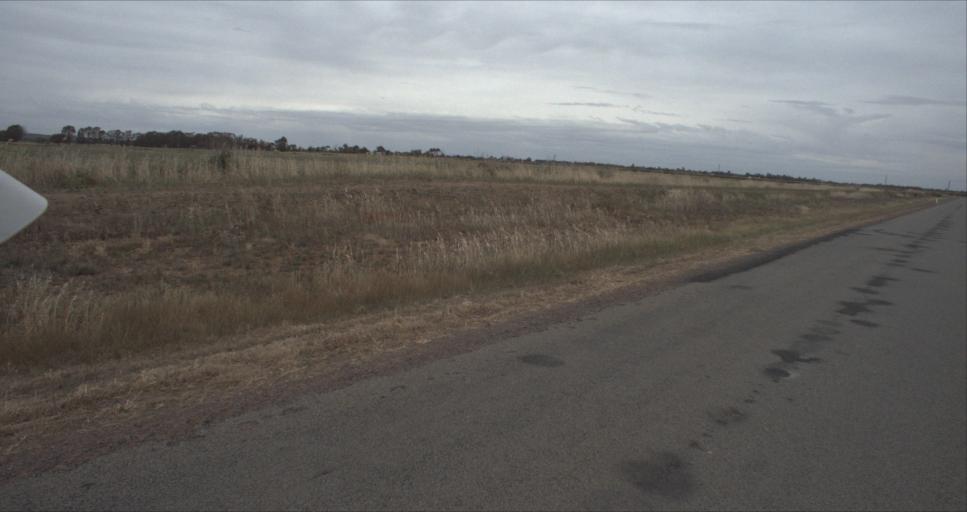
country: AU
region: New South Wales
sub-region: Leeton
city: Leeton
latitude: -34.4976
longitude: 146.4003
